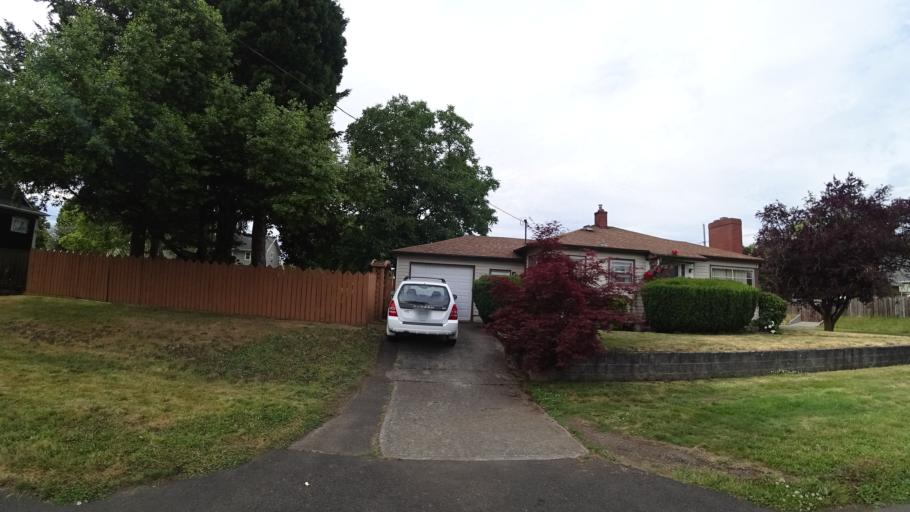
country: US
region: Oregon
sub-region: Multnomah County
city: Portland
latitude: 45.5736
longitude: -122.6986
